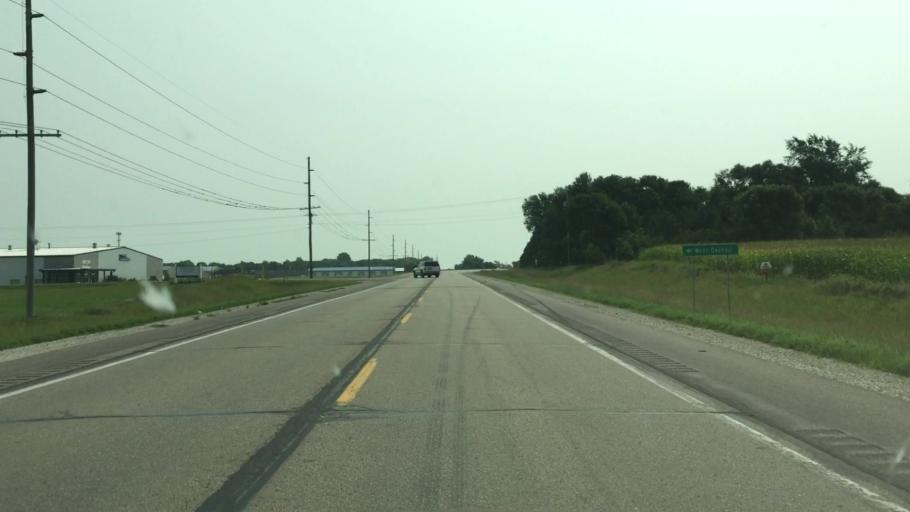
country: US
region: Iowa
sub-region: Dickinson County
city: Milford
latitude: 43.3424
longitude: -95.1612
